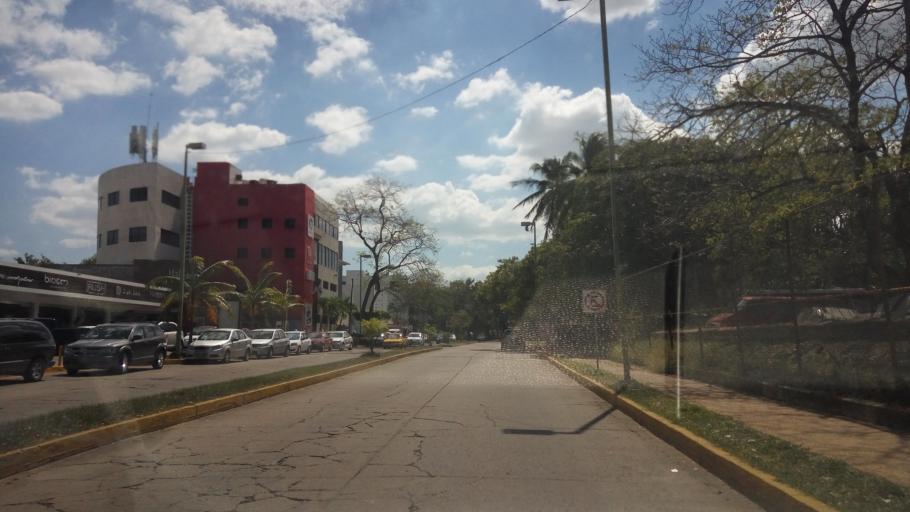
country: MX
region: Tabasco
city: Villahermosa
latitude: 18.0011
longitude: -92.9419
